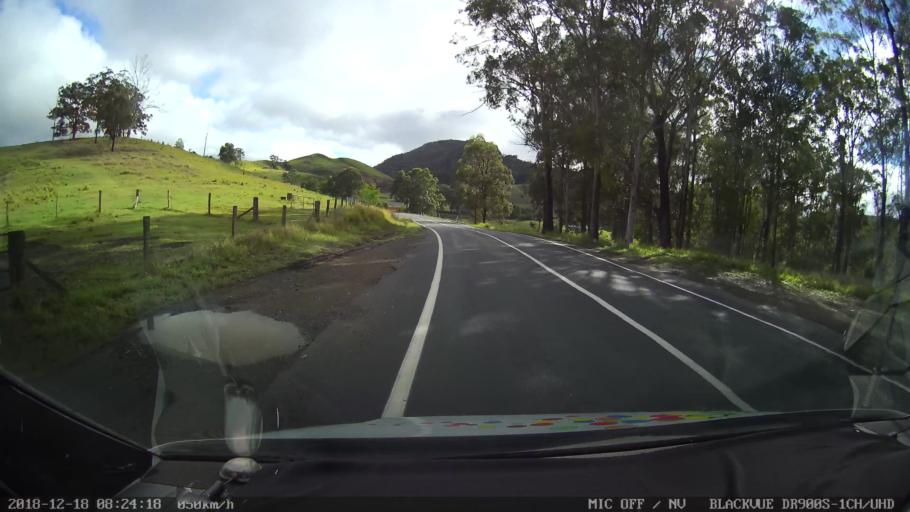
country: AU
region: New South Wales
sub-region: Kyogle
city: Kyogle
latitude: -28.3234
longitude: 152.7340
